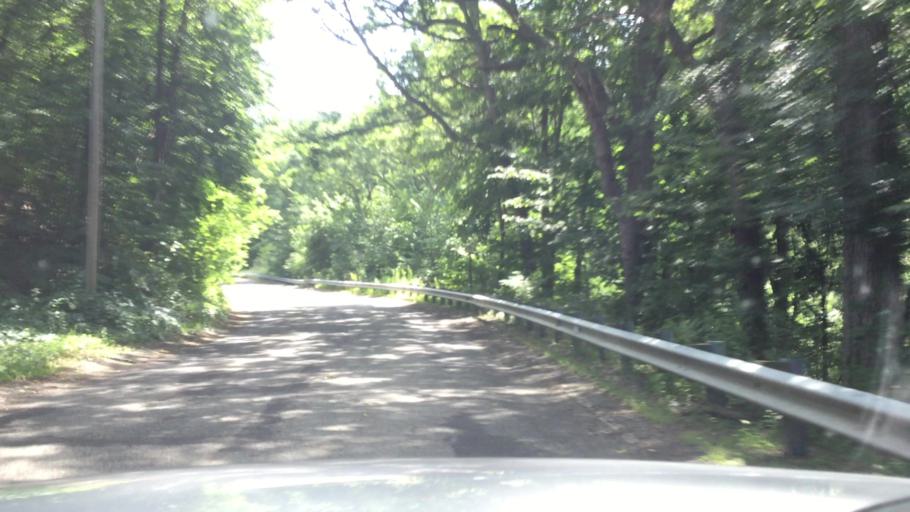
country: US
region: Michigan
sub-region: Ionia County
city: Belding
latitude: 43.1012
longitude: -85.2380
